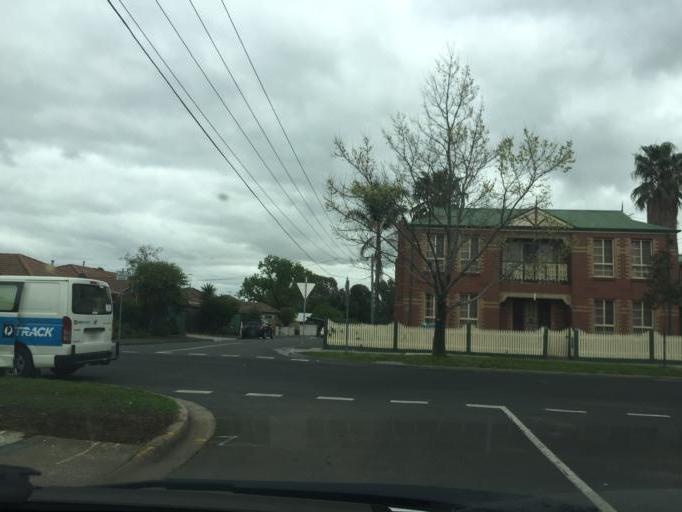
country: AU
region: Victoria
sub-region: Maribyrnong
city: Kingsville
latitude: -37.8175
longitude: 144.8796
